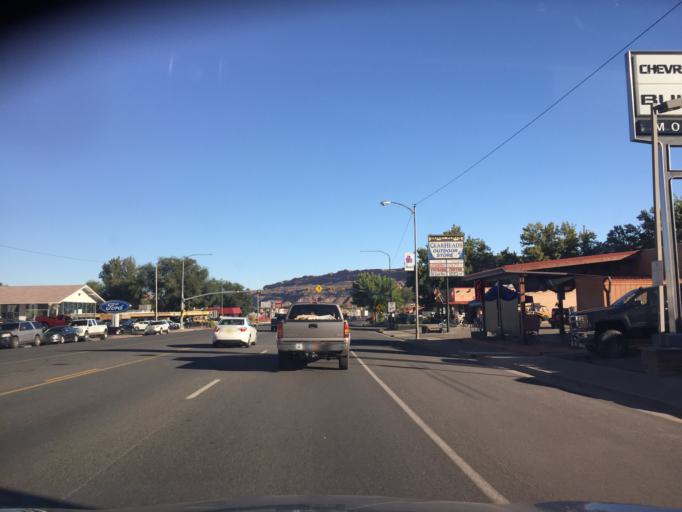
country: US
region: Utah
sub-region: Grand County
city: Moab
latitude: 38.5654
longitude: -109.5501
